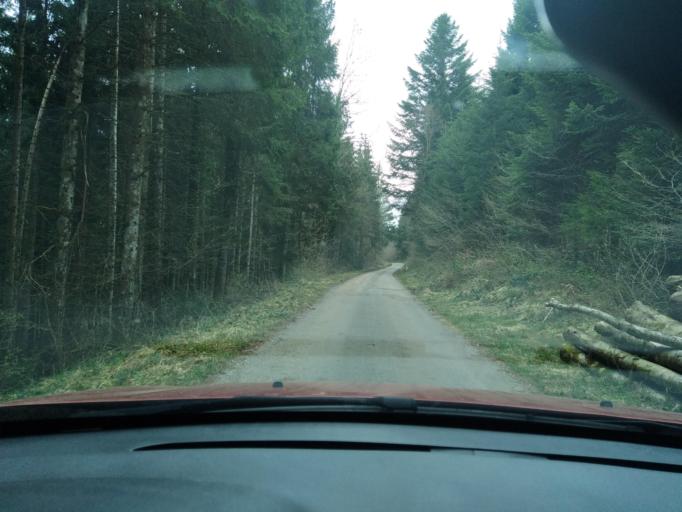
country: FR
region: Franche-Comte
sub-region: Departement du Jura
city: Moirans-en-Montagne
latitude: 46.4647
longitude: 5.7621
